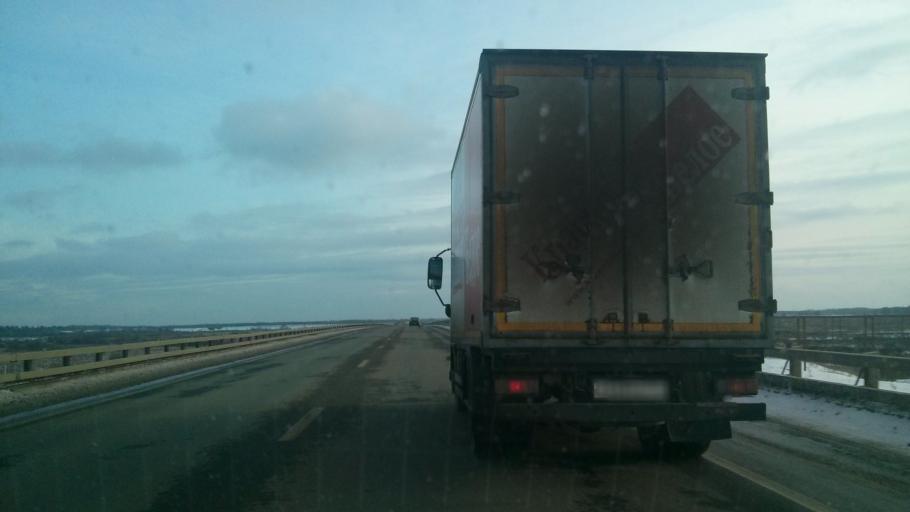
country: RU
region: Vladimir
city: Murom
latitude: 55.5961
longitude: 42.1092
